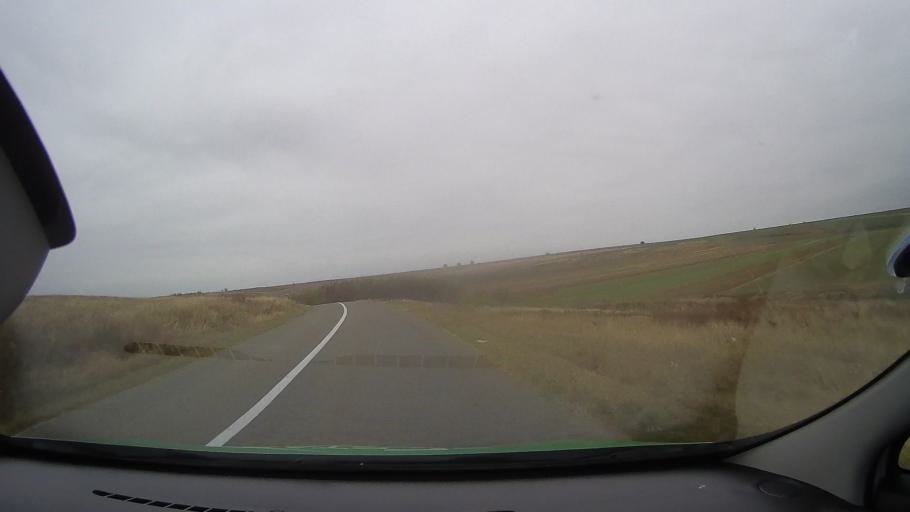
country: RO
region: Constanta
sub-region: Comuna Saraiu
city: Saraiu
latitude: 44.7259
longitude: 28.1809
